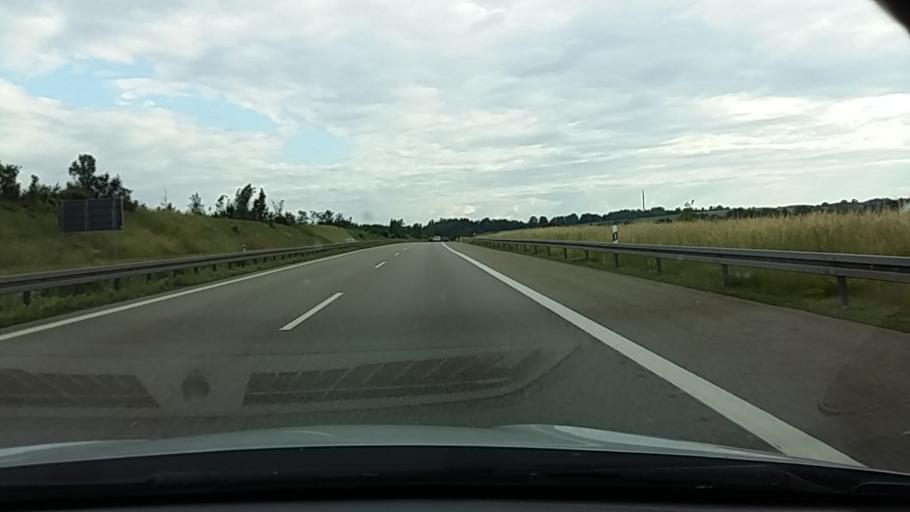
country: DE
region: Bavaria
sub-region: Upper Palatinate
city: Vohenstrauss
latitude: 49.6030
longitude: 12.3240
